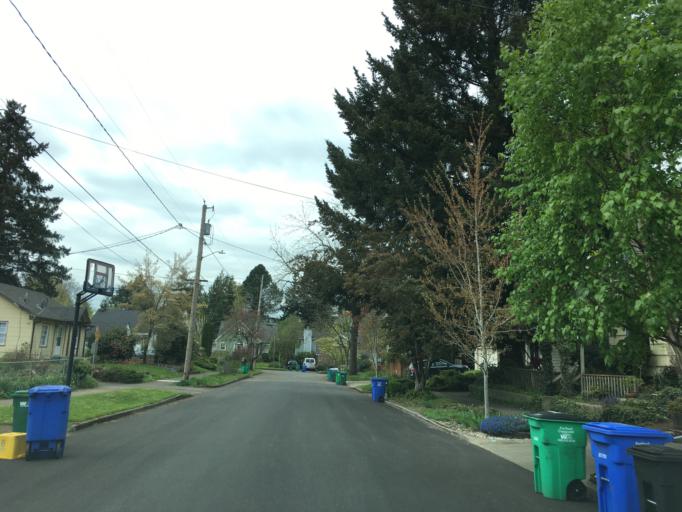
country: US
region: Oregon
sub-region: Multnomah County
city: Lents
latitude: 45.5254
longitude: -122.5959
